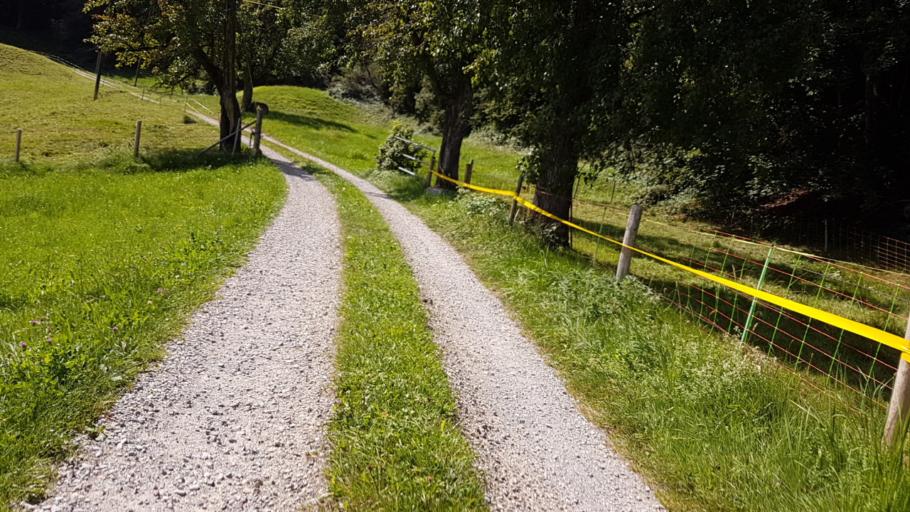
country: CH
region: Bern
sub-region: Bern-Mittelland District
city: Linden
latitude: 46.8406
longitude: 7.7141
